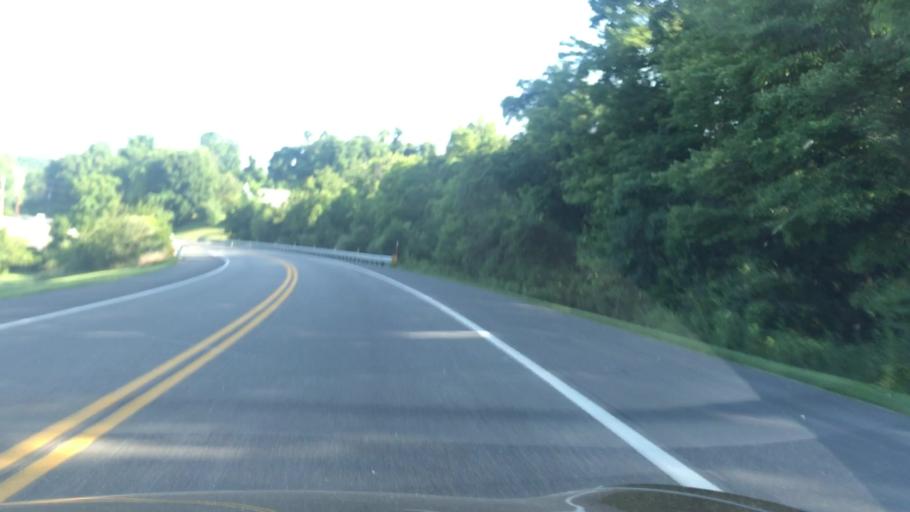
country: US
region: Pennsylvania
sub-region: Cumberland County
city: Lower Allen
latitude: 40.1643
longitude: -76.8850
